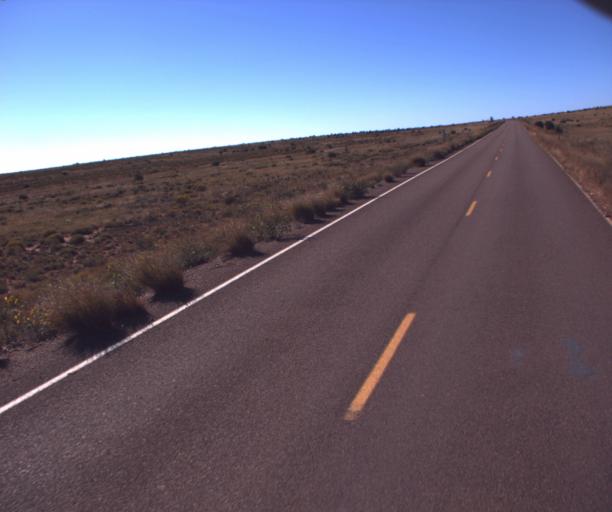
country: US
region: Arizona
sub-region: Navajo County
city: Heber-Overgaard
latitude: 34.4925
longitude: -110.3406
